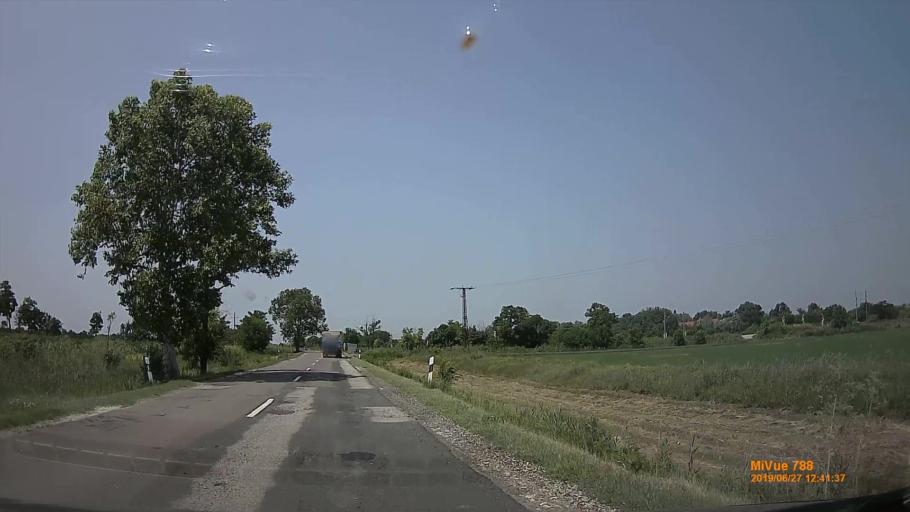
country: HU
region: Pest
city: Tortel
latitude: 47.1812
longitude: 19.8946
